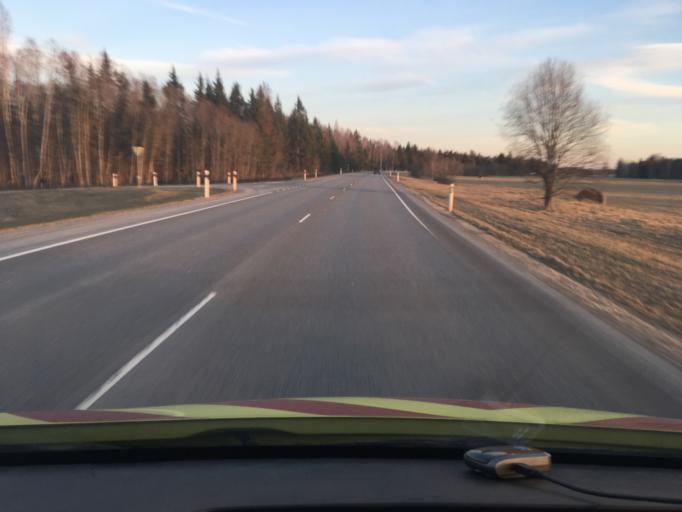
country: EE
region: Raplamaa
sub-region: Kohila vald
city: Kohila
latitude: 59.2308
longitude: 24.7744
